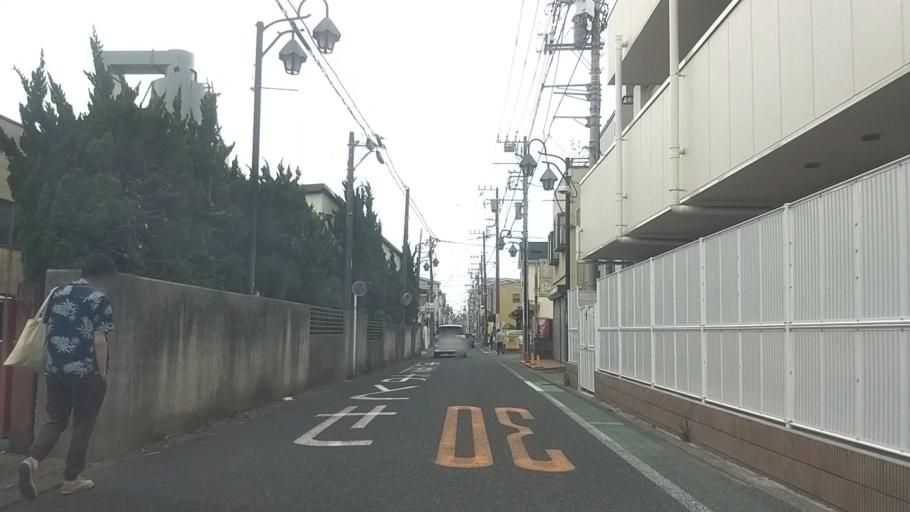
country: JP
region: Kanagawa
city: Fujisawa
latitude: 35.3404
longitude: 139.4519
